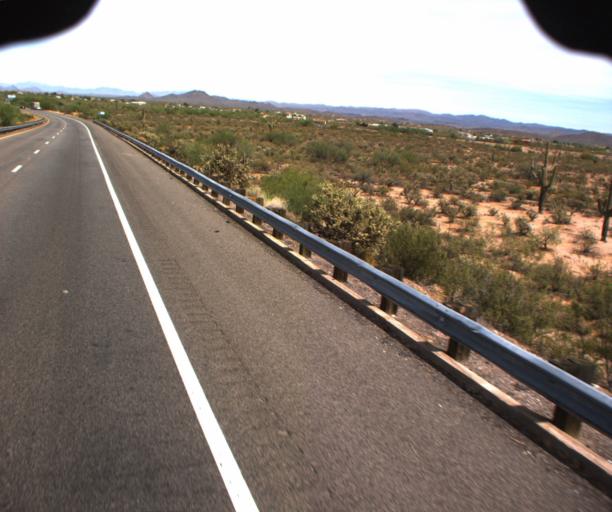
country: US
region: Arizona
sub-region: Maricopa County
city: Wickenburg
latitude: 33.8446
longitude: -112.6117
